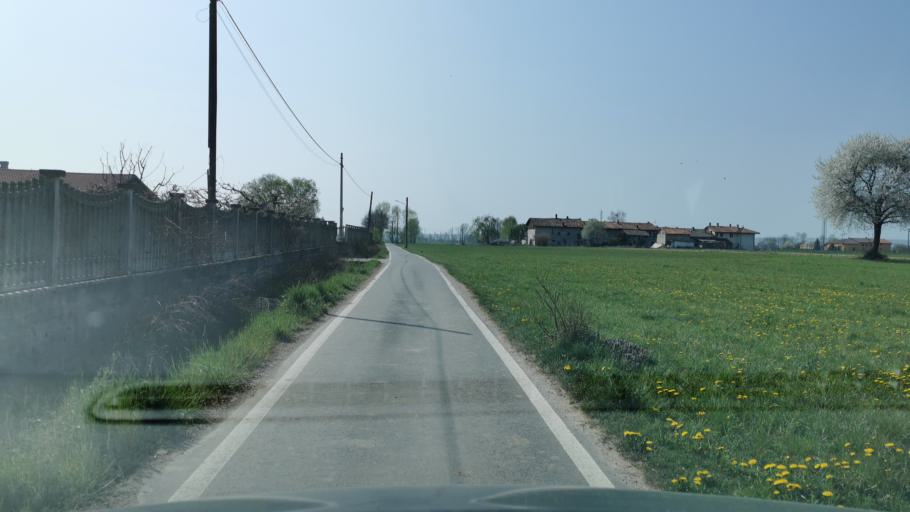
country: IT
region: Piedmont
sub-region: Provincia di Torino
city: Rivarolo Canavese
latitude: 45.3257
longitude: 7.7056
